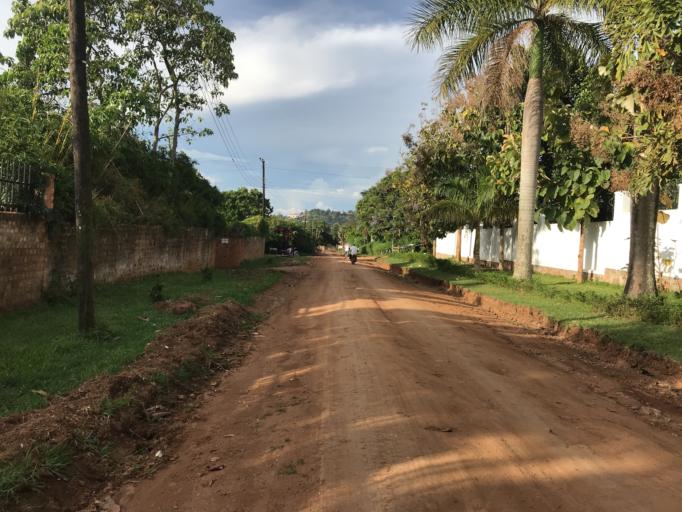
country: UG
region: Central Region
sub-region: Wakiso District
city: Entebbe
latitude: 0.0478
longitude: 32.4605
